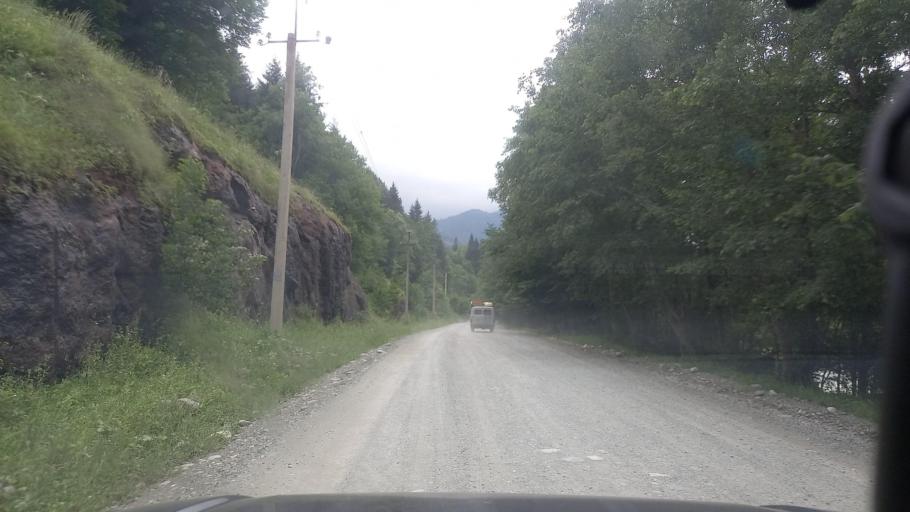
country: RU
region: Karachayevo-Cherkesiya
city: Kurdzhinovo
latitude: 43.8130
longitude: 40.9129
